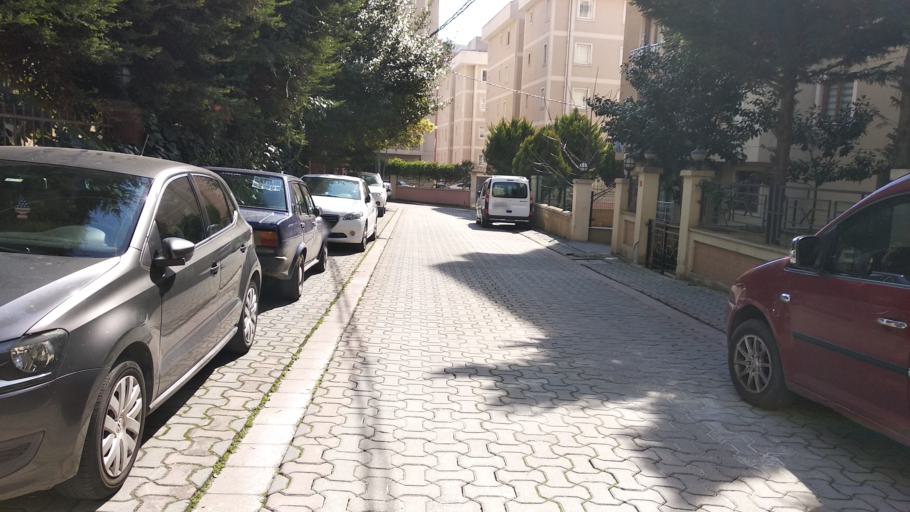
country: TR
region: Istanbul
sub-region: Atasehir
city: Atasehir
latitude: 40.9803
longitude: 29.1110
